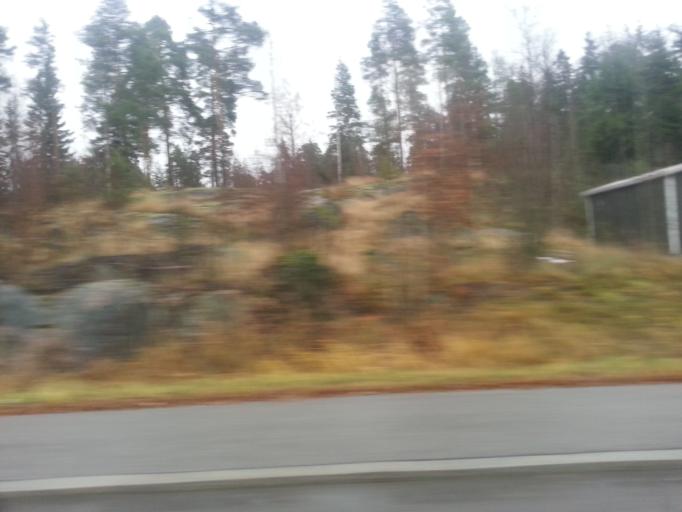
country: FI
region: Uusimaa
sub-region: Helsinki
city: Vantaa
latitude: 60.3001
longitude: 24.9514
